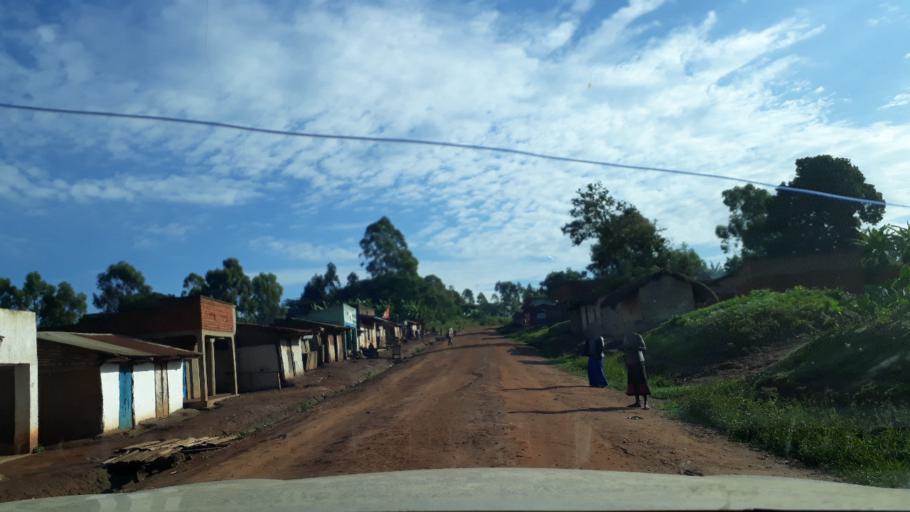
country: UG
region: Northern Region
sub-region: Zombo District
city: Paidha
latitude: 2.2763
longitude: 30.9570
